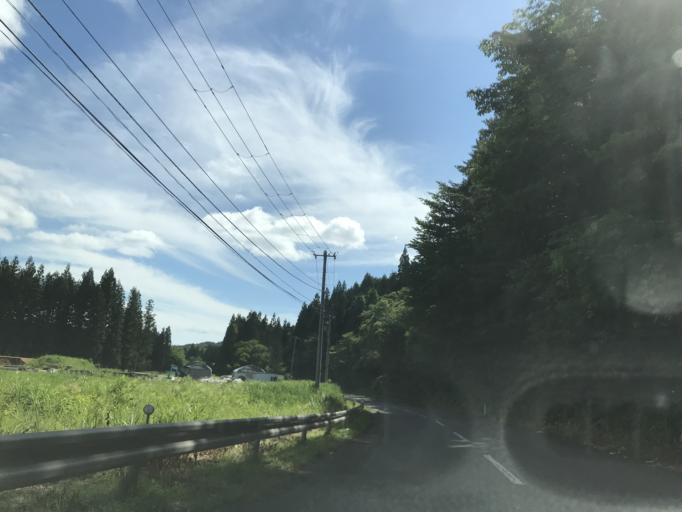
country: JP
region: Iwate
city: Ichinoseki
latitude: 38.9505
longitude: 140.9291
